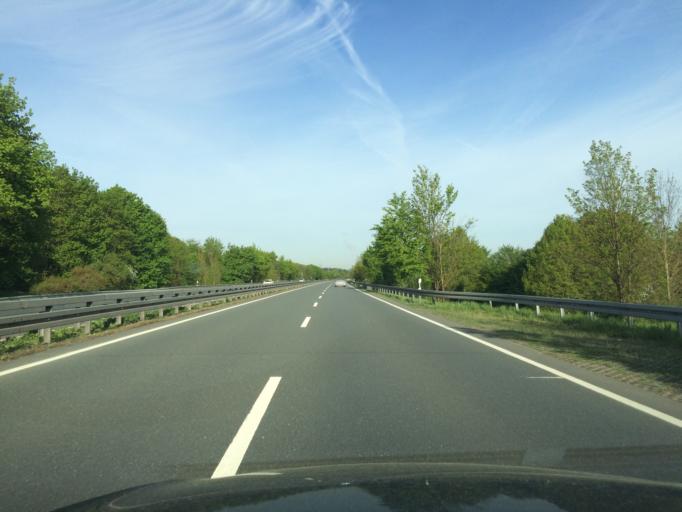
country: DE
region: Bavaria
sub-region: Regierungsbezirk Unterfranken
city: Gerbrunn
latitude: 49.7853
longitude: 10.0141
